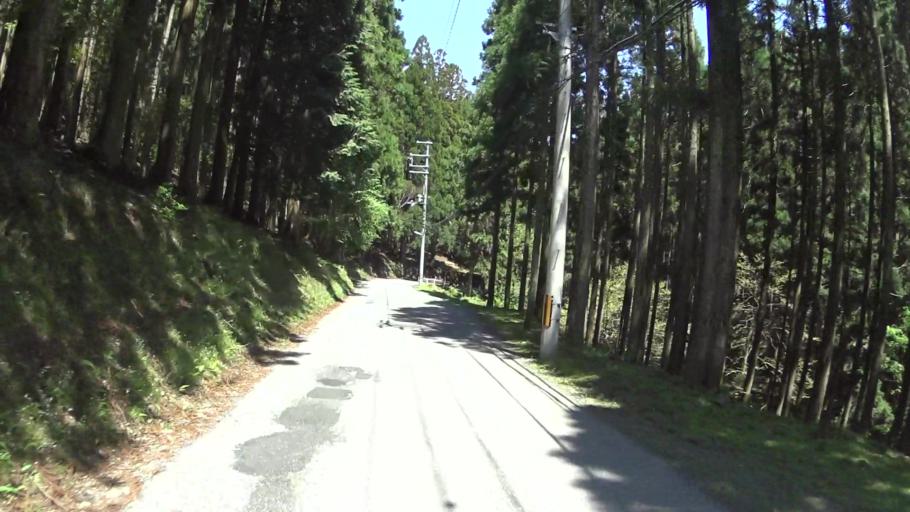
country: JP
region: Shiga Prefecture
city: Kitahama
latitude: 35.1841
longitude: 135.7850
